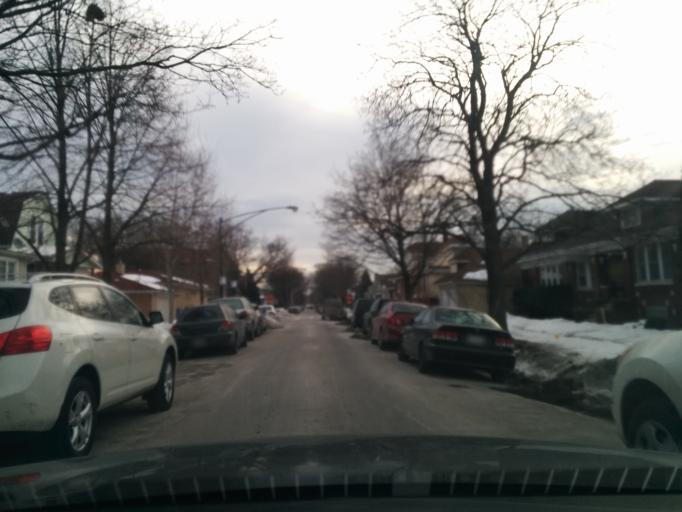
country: US
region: Illinois
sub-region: Cook County
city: Harwood Heights
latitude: 41.9478
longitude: -87.7605
